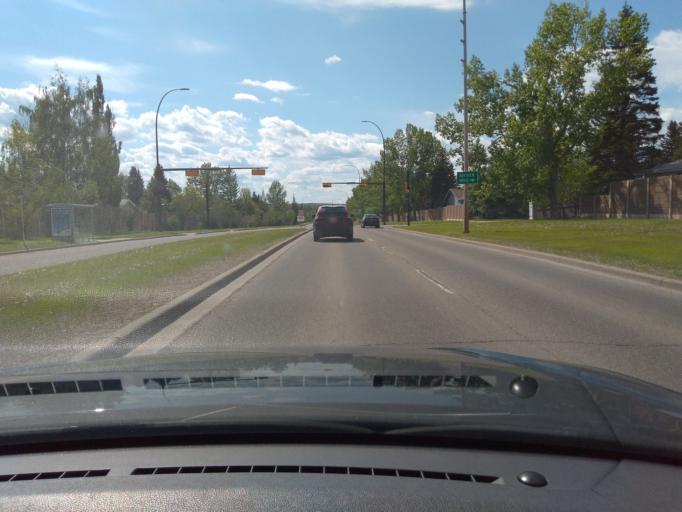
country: CA
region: Alberta
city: Calgary
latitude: 50.9722
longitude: -114.1108
